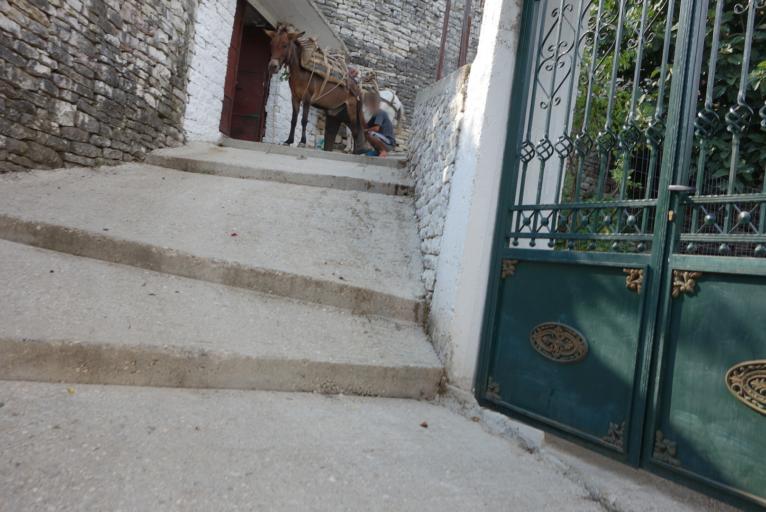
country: AL
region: Gjirokaster
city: Gjirokaster
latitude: 40.0696
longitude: 20.1328
